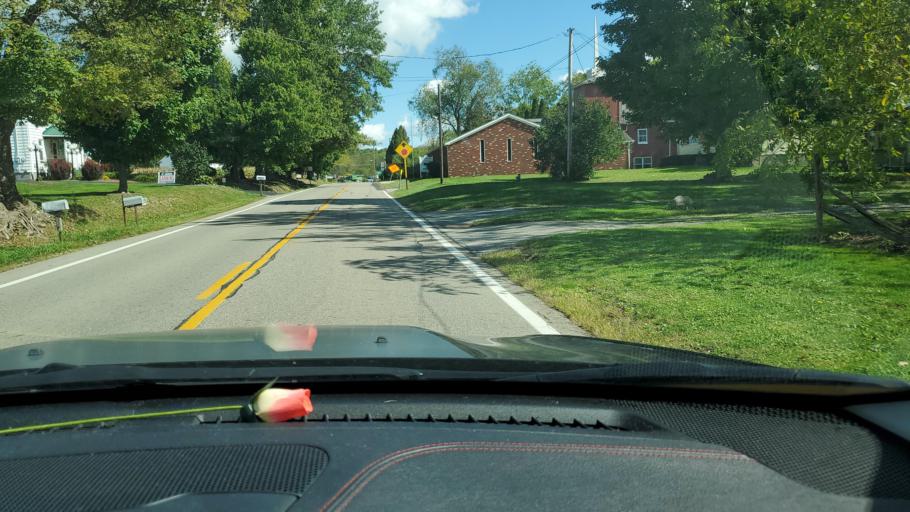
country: US
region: Ohio
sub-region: Ashtabula County
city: Andover
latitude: 41.4555
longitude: -80.5825
